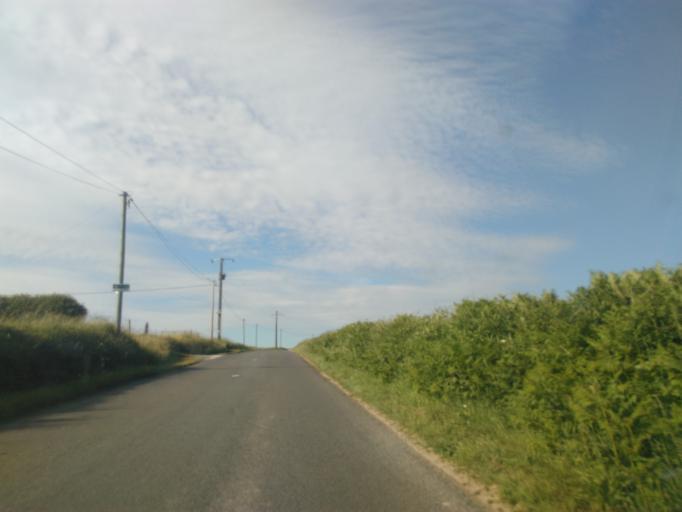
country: FR
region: Brittany
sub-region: Departement d'Ille-et-Vilaine
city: Romille
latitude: 48.2012
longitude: -1.9025
